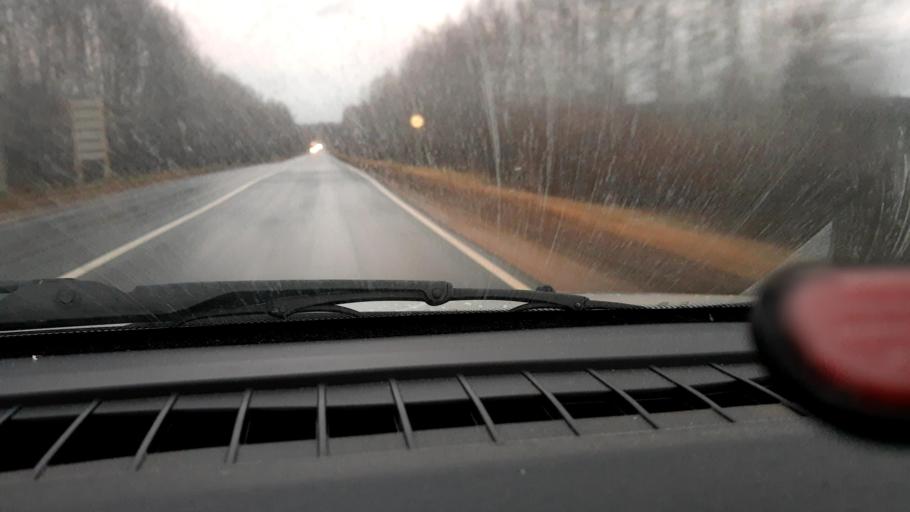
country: RU
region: Nizjnij Novgorod
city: Uren'
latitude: 57.2447
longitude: 45.5857
